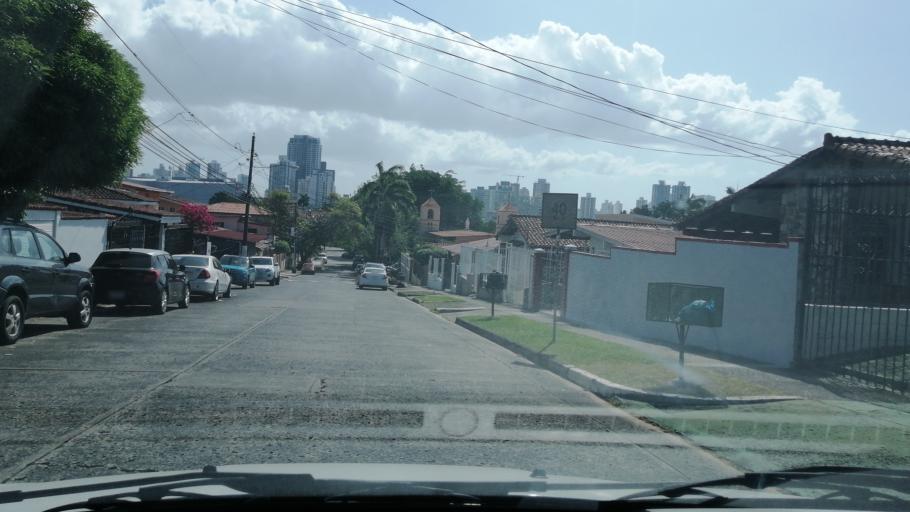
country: PA
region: Panama
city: Panama
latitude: 9.0063
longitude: -79.5259
